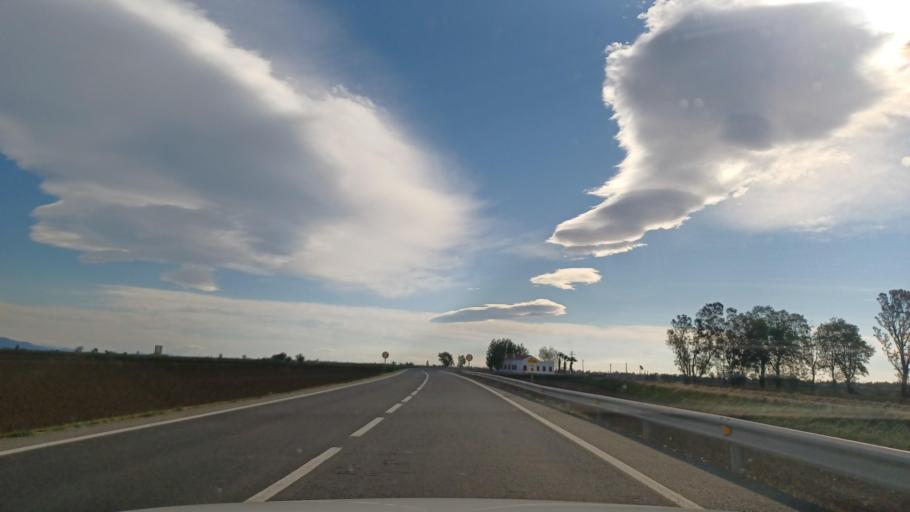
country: ES
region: Catalonia
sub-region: Provincia de Tarragona
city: Deltebre
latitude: 40.7211
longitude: 0.6514
